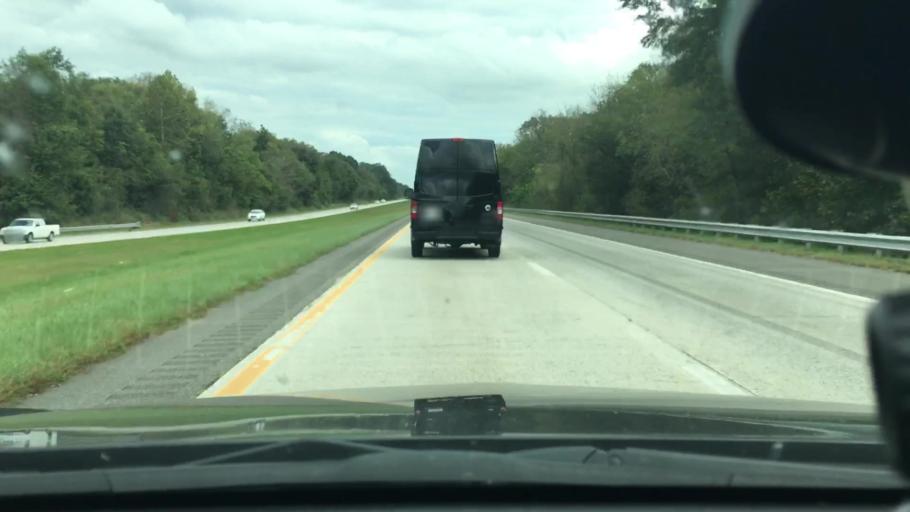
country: US
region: North Carolina
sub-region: Iredell County
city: Statesville
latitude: 35.8524
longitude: -80.7537
